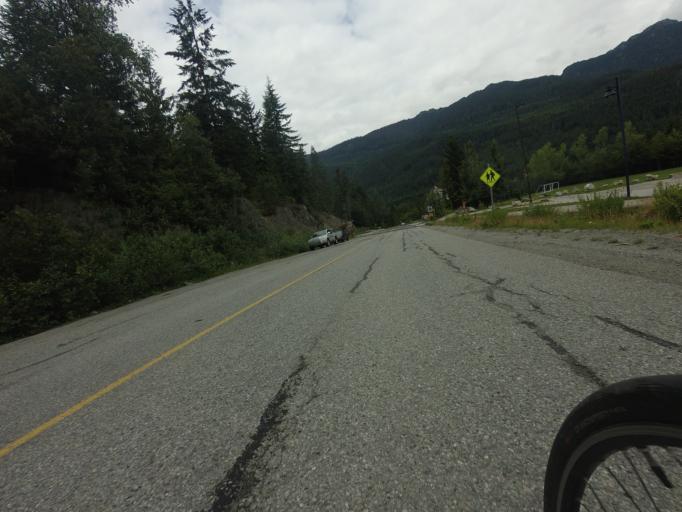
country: CA
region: British Columbia
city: Whistler
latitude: 50.0859
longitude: -123.0232
